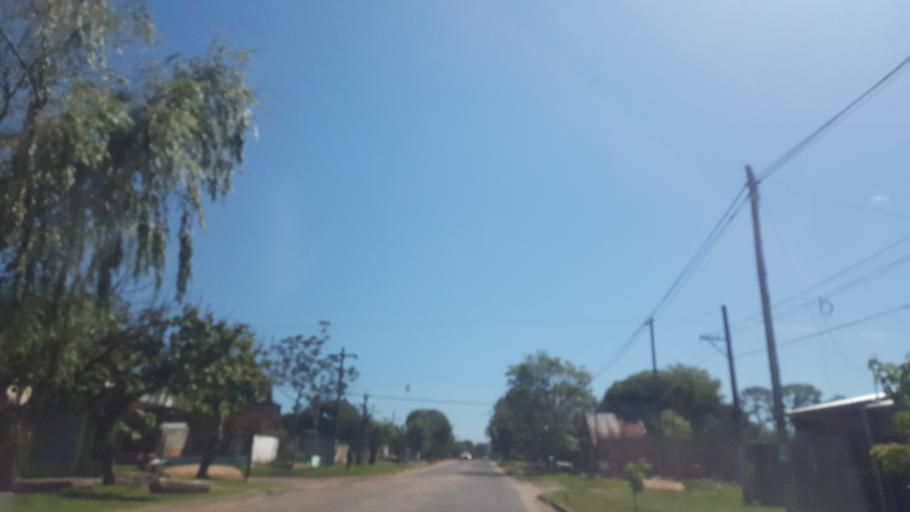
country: AR
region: Corrientes
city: Ituzaingo
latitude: -27.5935
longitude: -56.6942
